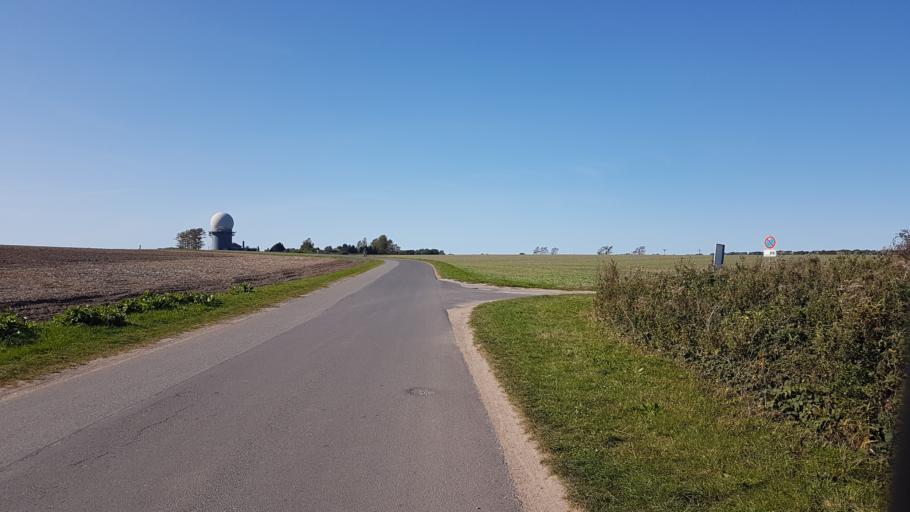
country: DE
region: Mecklenburg-Vorpommern
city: Altenkirchen
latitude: 54.6726
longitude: 13.3969
